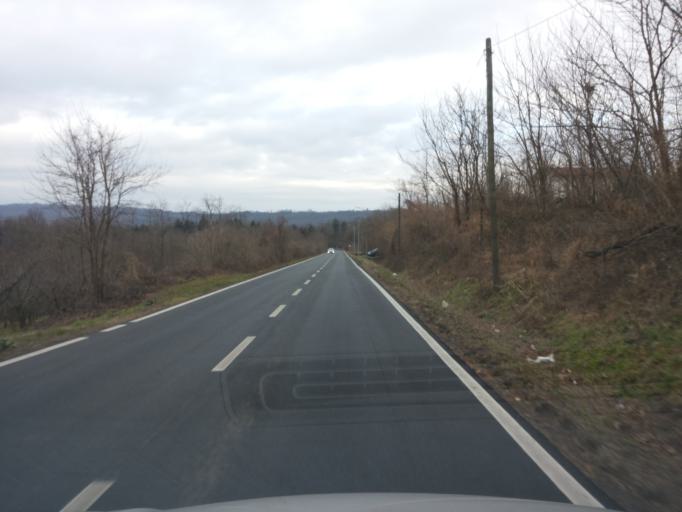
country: IT
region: Piedmont
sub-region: Provincia di Vercelli
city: Moncrivello
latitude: 45.3399
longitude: 7.9954
